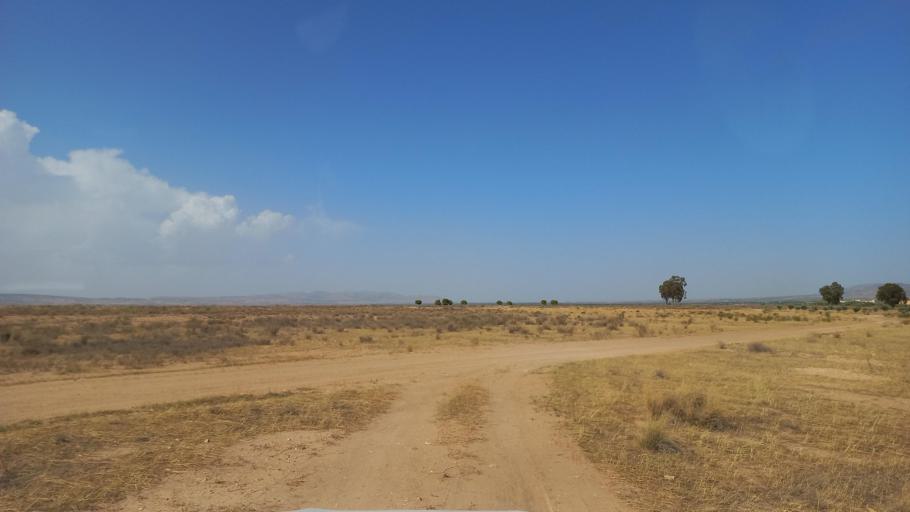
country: TN
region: Al Qasrayn
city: Kasserine
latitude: 35.2154
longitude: 9.0321
